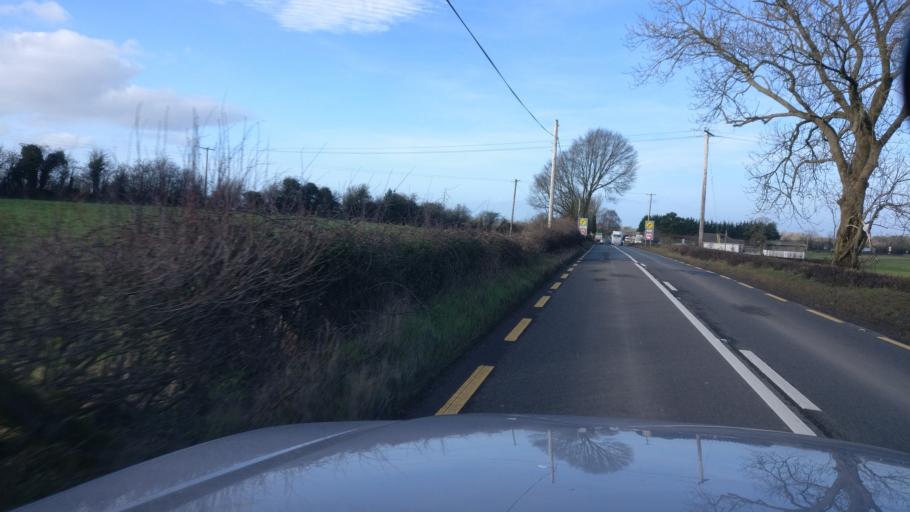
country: IE
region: Leinster
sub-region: Laois
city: Mountmellick
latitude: 53.0981
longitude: -7.3381
